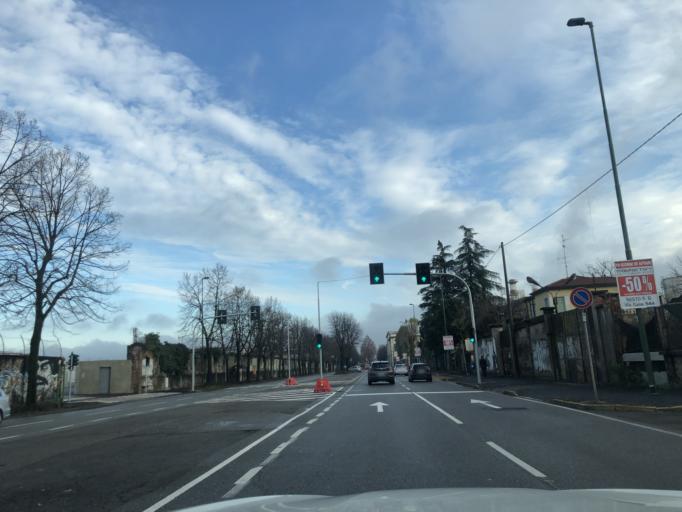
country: IT
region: Lombardy
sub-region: Citta metropolitana di Milano
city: Sesto San Giovanni
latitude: 45.5405
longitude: 9.2494
